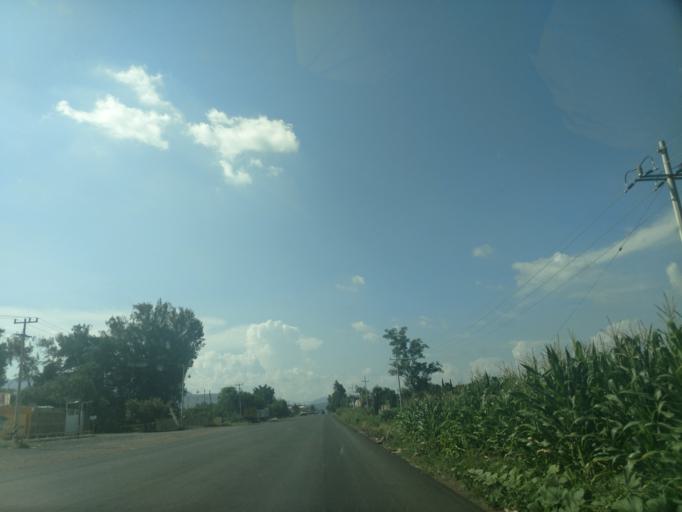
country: MX
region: Jalisco
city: Ahualulco de Mercado
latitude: 20.6980
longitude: -103.9643
